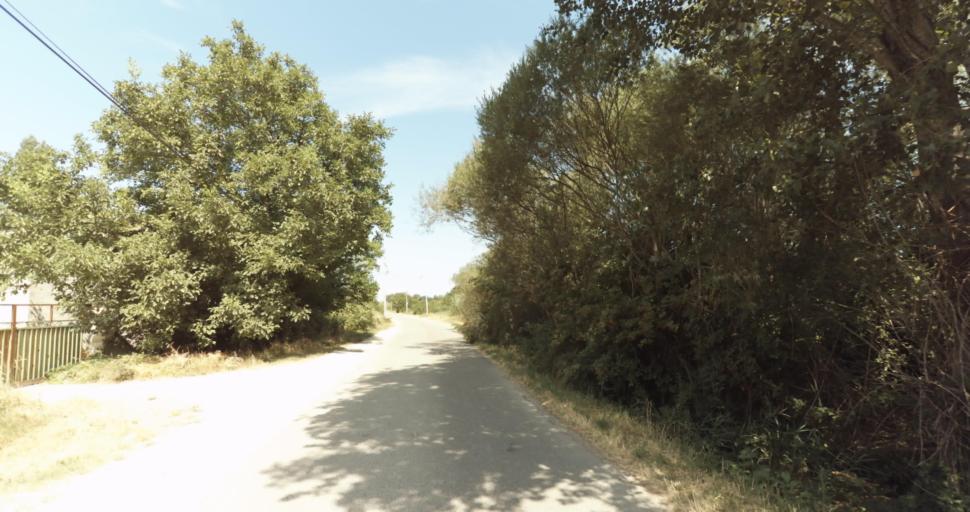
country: FR
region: Provence-Alpes-Cote d'Azur
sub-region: Departement du Vaucluse
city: Monteux
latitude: 44.0172
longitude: 4.9808
